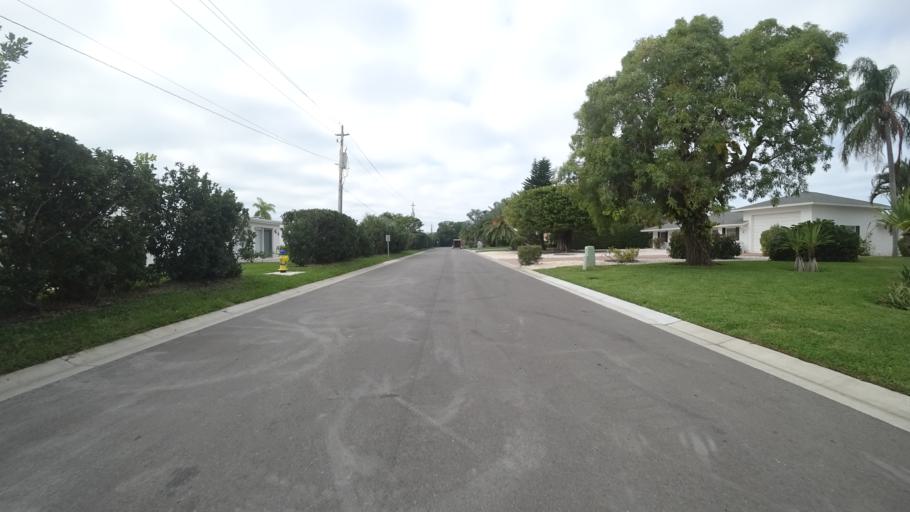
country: US
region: Florida
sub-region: Manatee County
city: Longboat Key
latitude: 27.4202
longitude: -82.6601
